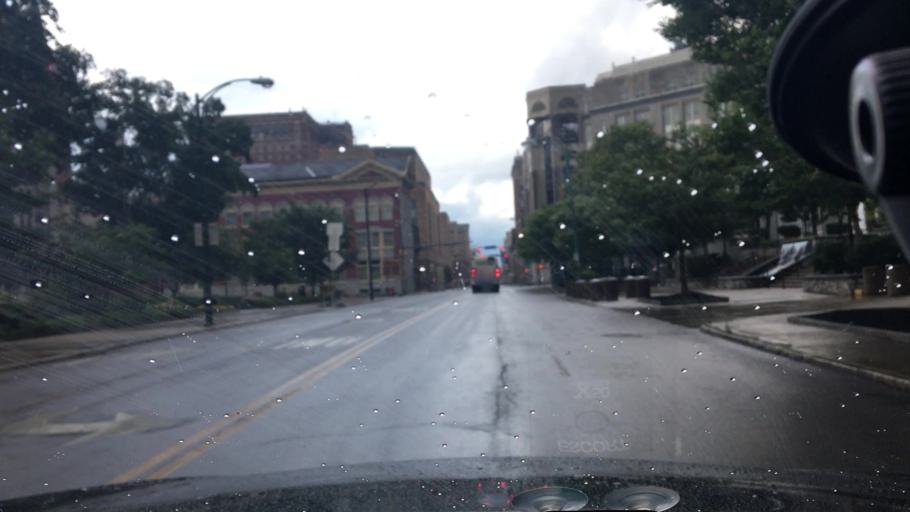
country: US
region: New York
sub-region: Erie County
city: Buffalo
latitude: 42.8837
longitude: -78.8773
